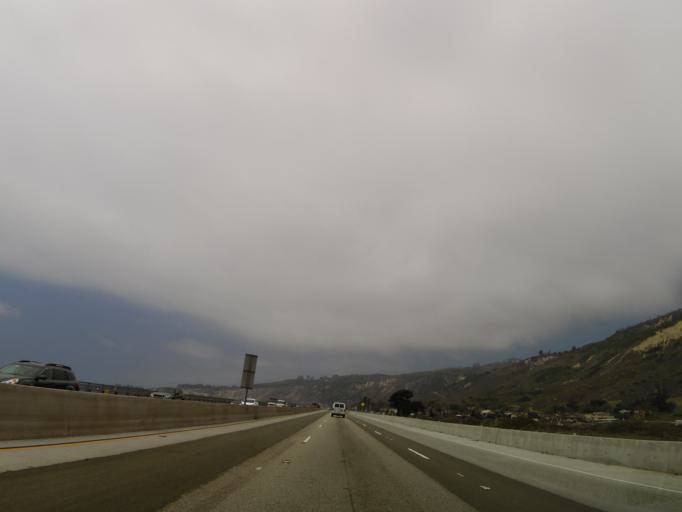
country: US
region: California
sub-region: Santa Barbara County
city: Carpinteria
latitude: 34.3575
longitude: -119.4431
